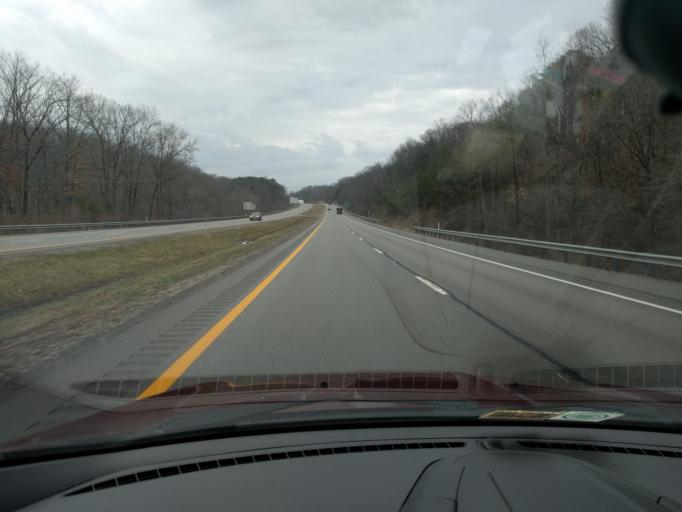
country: US
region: West Virginia
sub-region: Wood County
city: Boaz
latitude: 39.3199
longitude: -81.4724
